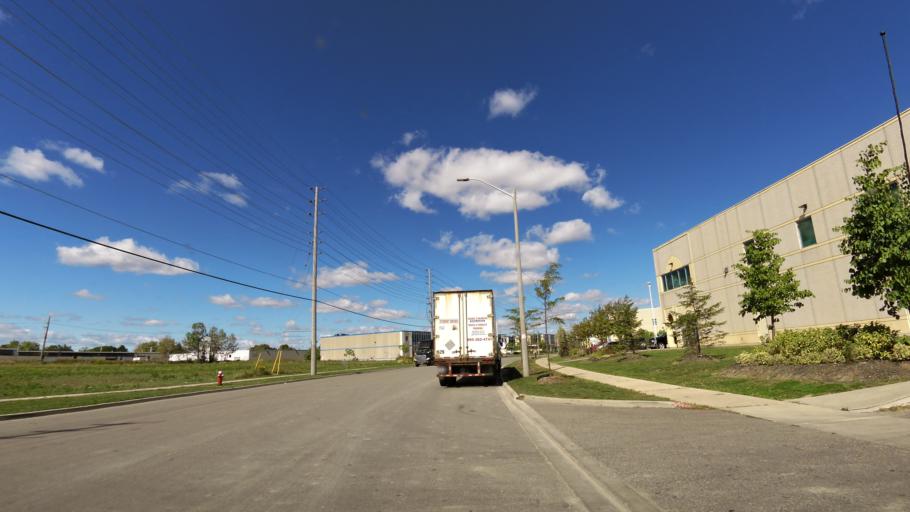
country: CA
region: Ontario
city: Etobicoke
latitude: 43.7086
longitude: -79.6543
